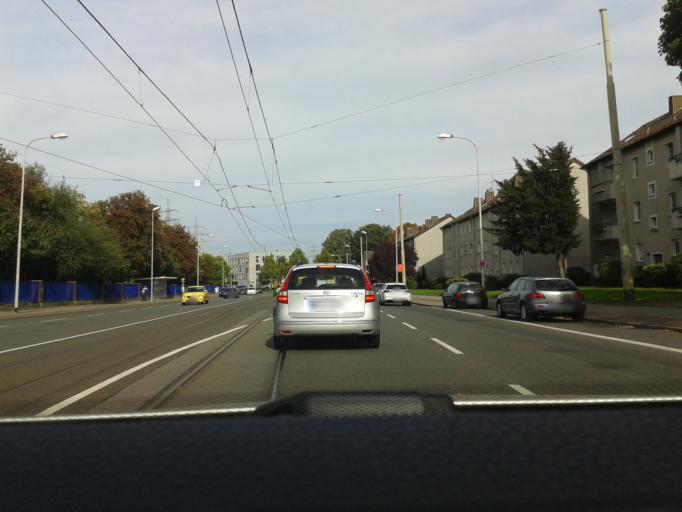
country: DE
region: North Rhine-Westphalia
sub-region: Regierungsbezirk Dusseldorf
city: Muelheim (Ruhr)
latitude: 51.4475
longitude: 6.8837
